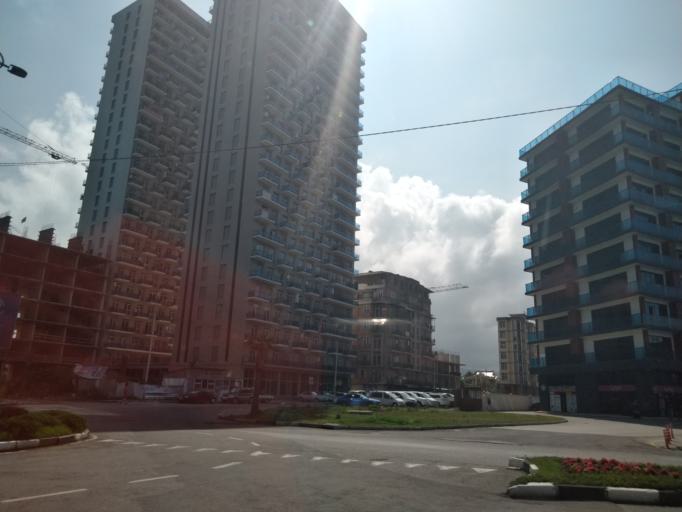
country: GE
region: Ajaria
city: Batumi
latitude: 41.6293
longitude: 41.6022
